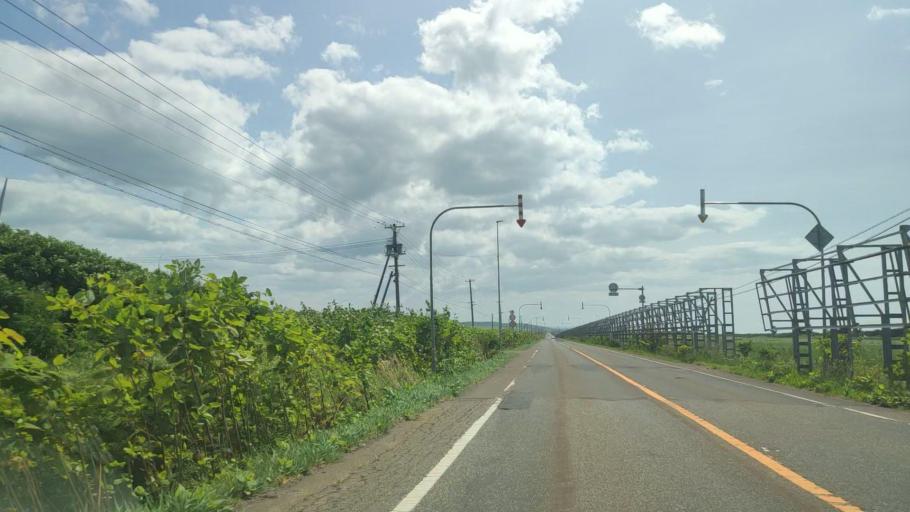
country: JP
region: Hokkaido
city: Makubetsu
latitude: 44.7090
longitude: 141.7897
